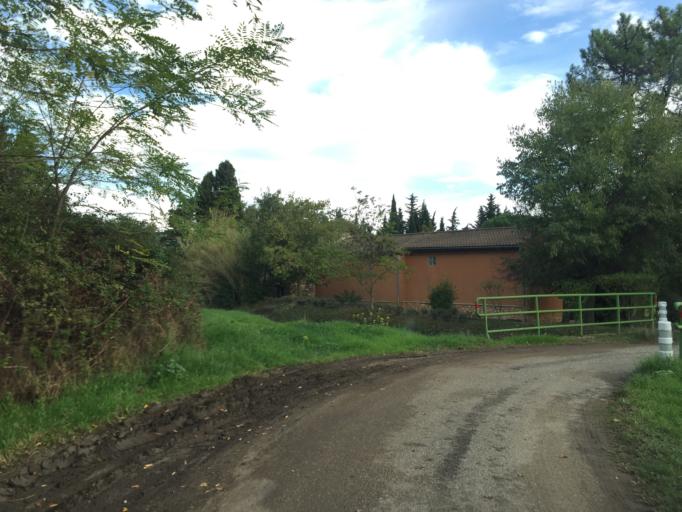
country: FR
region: Provence-Alpes-Cote d'Azur
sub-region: Departement du Vaucluse
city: Orange
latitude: 44.1118
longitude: 4.8101
